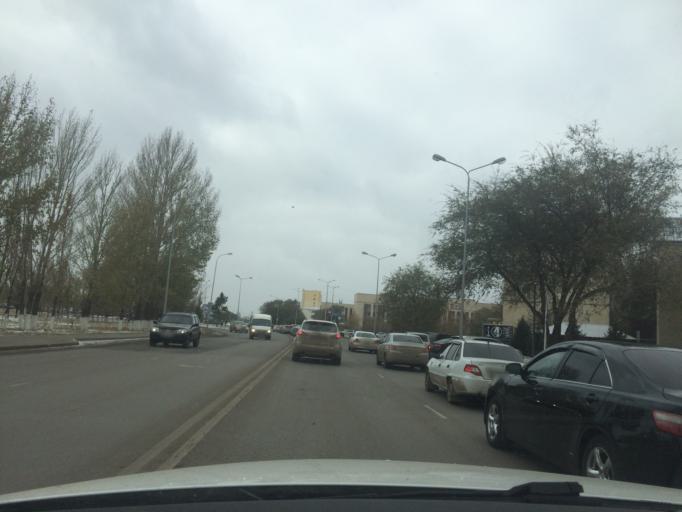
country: KZ
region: Astana Qalasy
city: Astana
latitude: 51.1561
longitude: 71.4557
